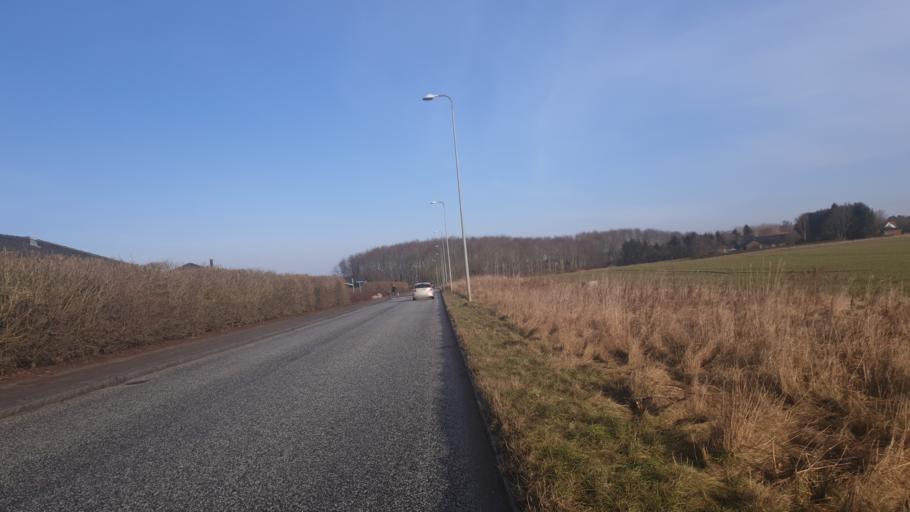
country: DK
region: Central Jutland
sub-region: Hedensted Kommune
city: Hedensted
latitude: 55.7705
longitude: 9.7199
